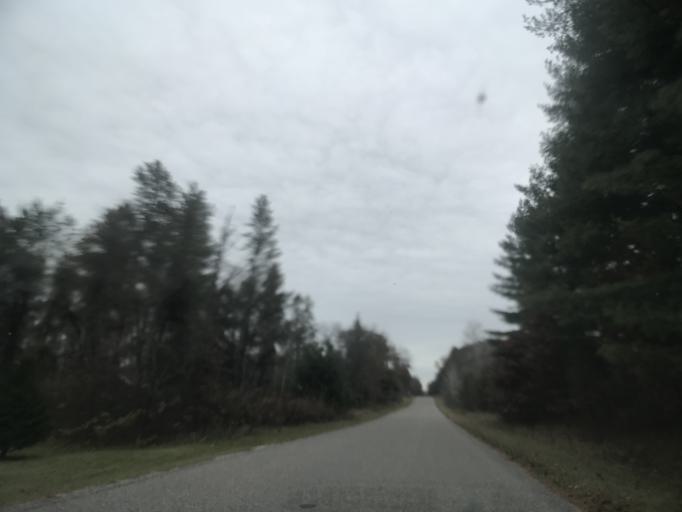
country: US
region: Wisconsin
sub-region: Oconto County
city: Gillett
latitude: 45.3464
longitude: -88.2860
